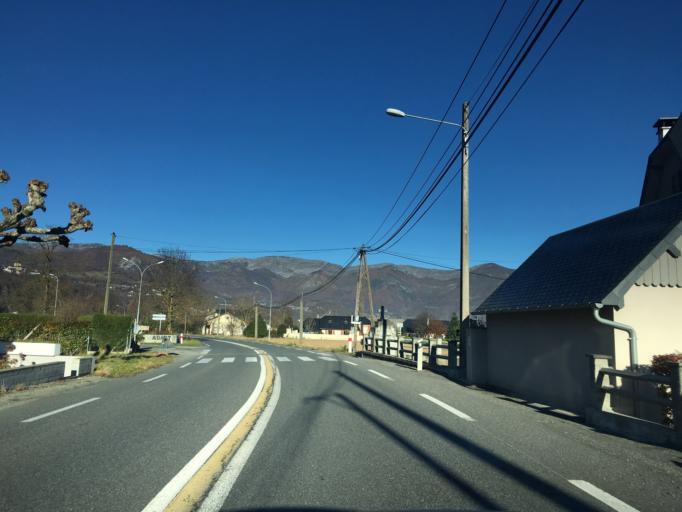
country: FR
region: Midi-Pyrenees
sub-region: Departement des Hautes-Pyrenees
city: Pierrefitte-Nestalas
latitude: 42.9736
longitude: -0.0760
